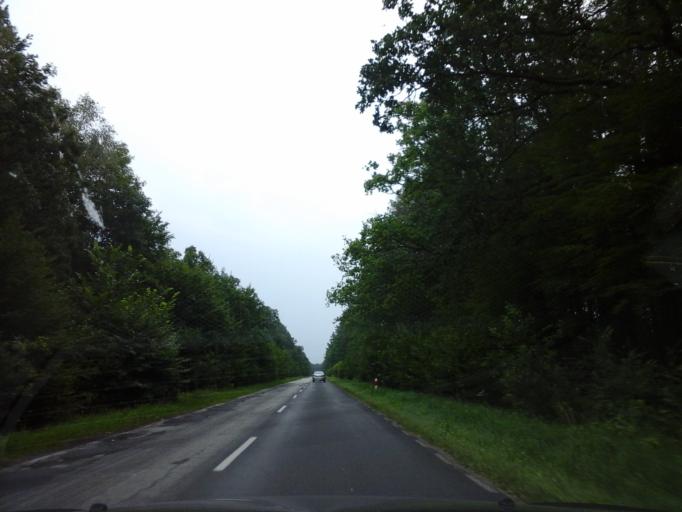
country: PL
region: Lubusz
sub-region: Powiat strzelecko-drezdenecki
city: Drezdenko
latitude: 52.8057
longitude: 15.8305
